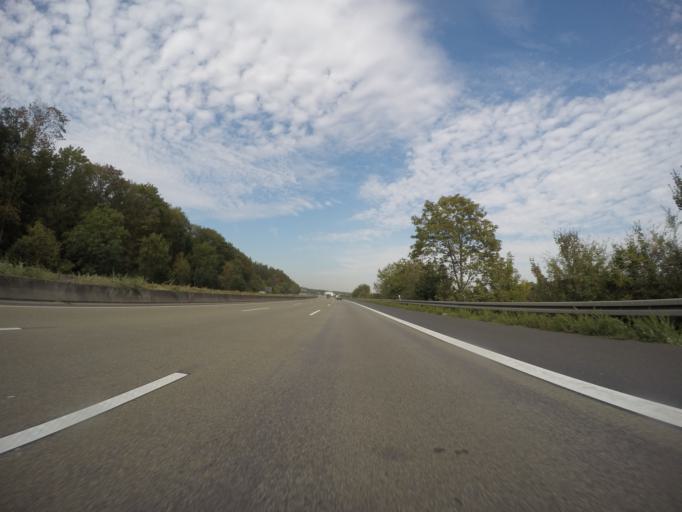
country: DE
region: Hesse
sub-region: Regierungsbezirk Darmstadt
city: Seligenstadt
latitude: 50.0441
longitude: 8.9314
